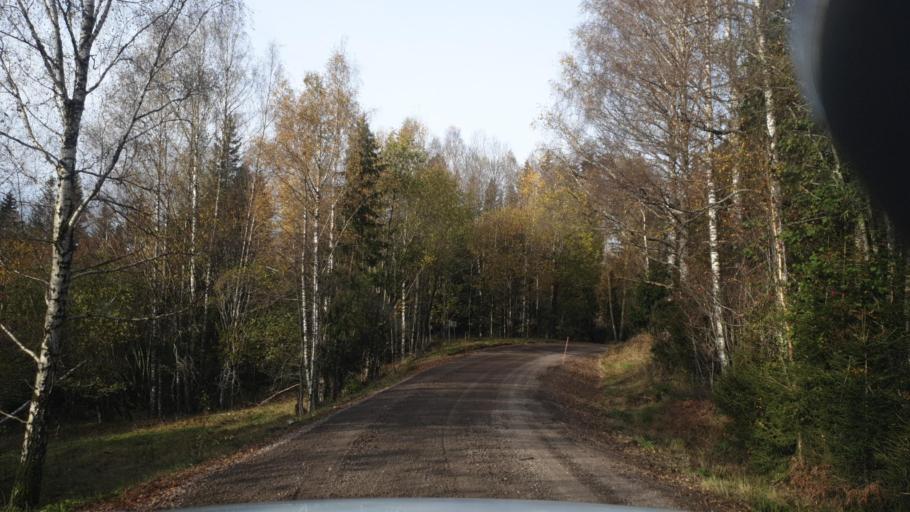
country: NO
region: Hedmark
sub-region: Eidskog
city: Skotterud
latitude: 59.7375
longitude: 12.0795
